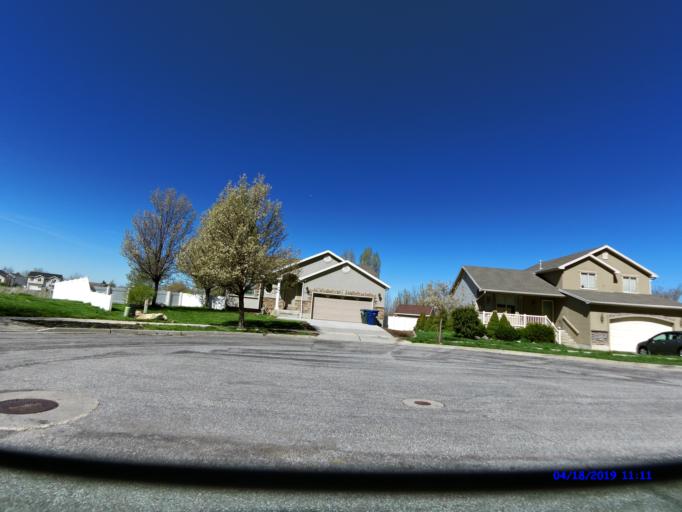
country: US
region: Utah
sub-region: Weber County
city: North Ogden
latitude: 41.2821
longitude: -111.9508
